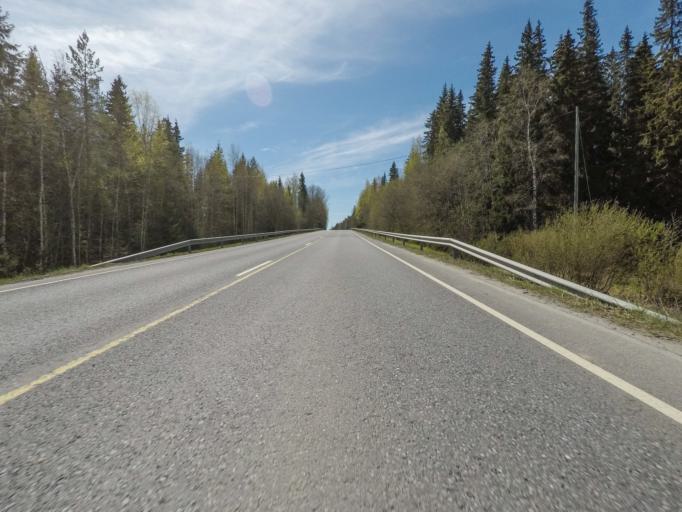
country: FI
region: Pirkanmaa
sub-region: Etelae-Pirkanmaa
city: Urjala
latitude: 61.0093
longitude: 23.4736
